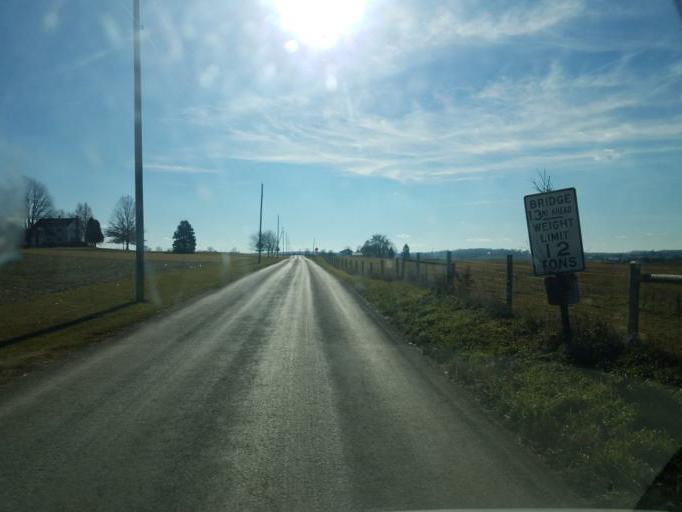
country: US
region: Ohio
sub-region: Wayne County
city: Apple Creek
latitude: 40.7407
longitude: -81.7752
